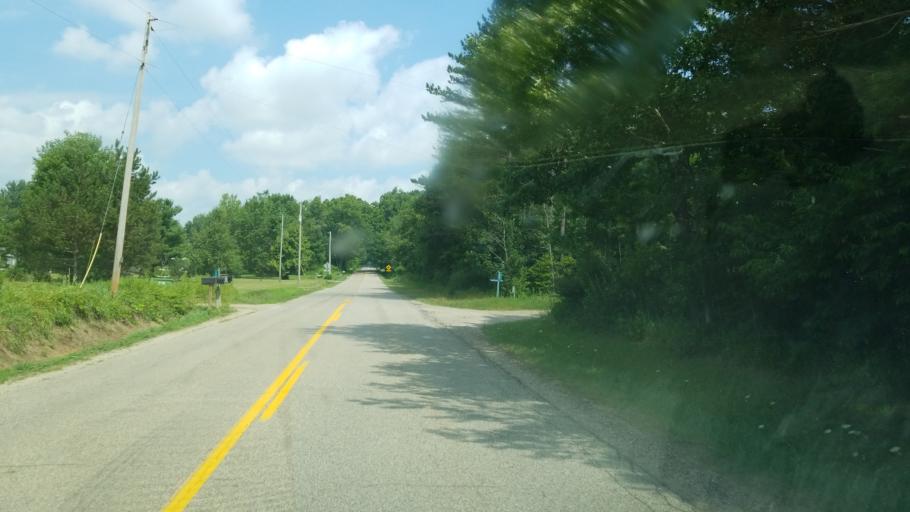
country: US
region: Michigan
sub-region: Kent County
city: Cedar Springs
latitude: 43.2466
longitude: -85.5112
